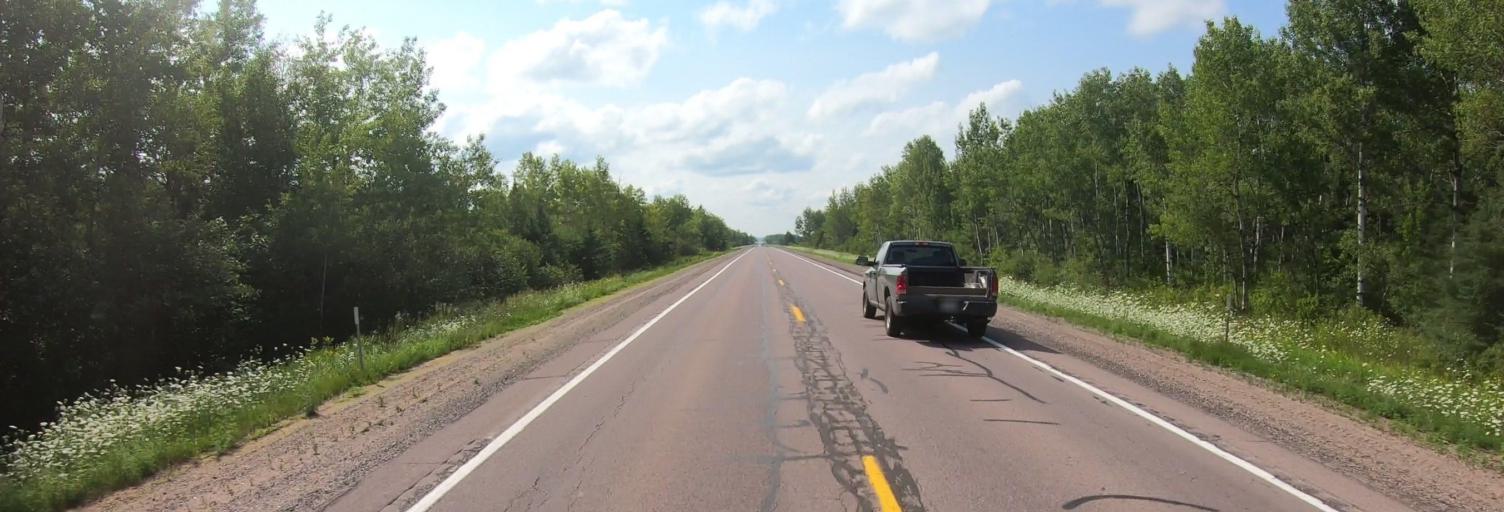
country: US
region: Michigan
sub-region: Ontonagon County
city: Ontonagon
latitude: 46.5473
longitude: -89.3565
